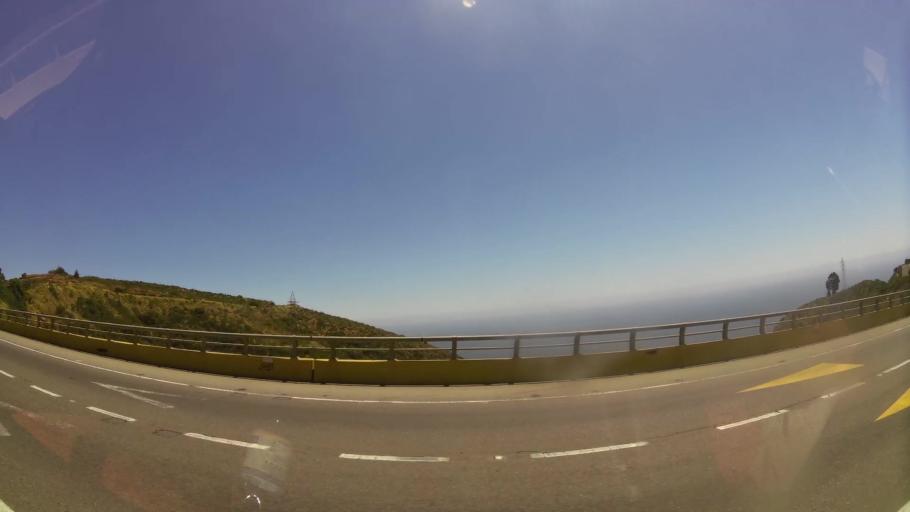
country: CL
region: Valparaiso
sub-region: Provincia de Valparaiso
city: Valparaiso
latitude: -33.0553
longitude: -71.6532
